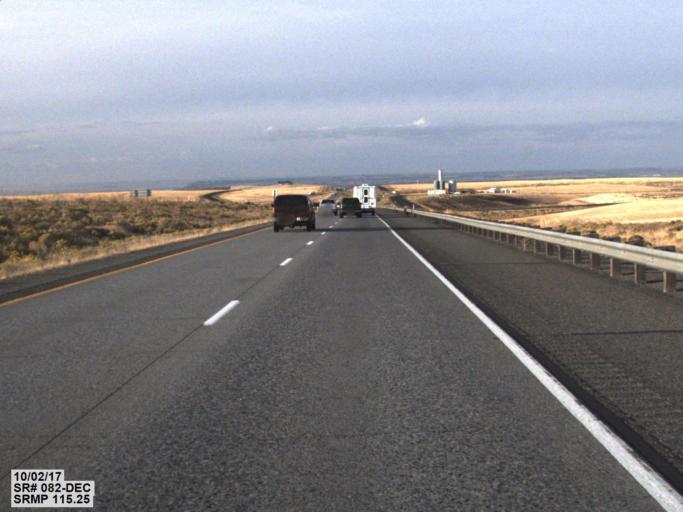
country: US
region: Washington
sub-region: Benton County
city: Highland
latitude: 46.1297
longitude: -119.2020
